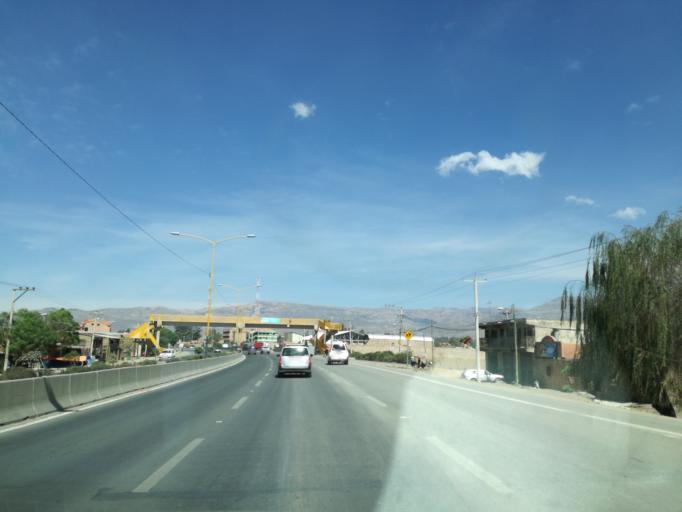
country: BO
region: Cochabamba
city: Sipe Sipe
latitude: -17.3989
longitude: -66.3265
